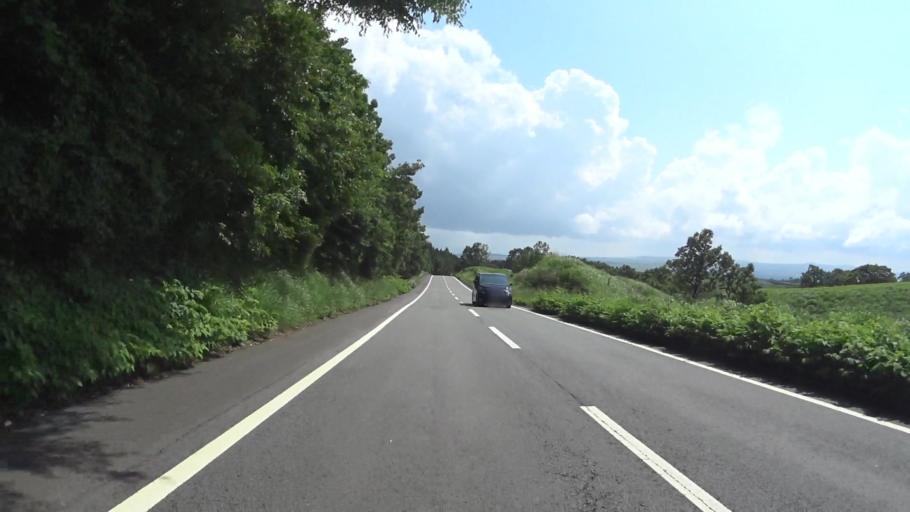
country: JP
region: Kumamoto
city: Aso
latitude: 33.0644
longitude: 131.1845
